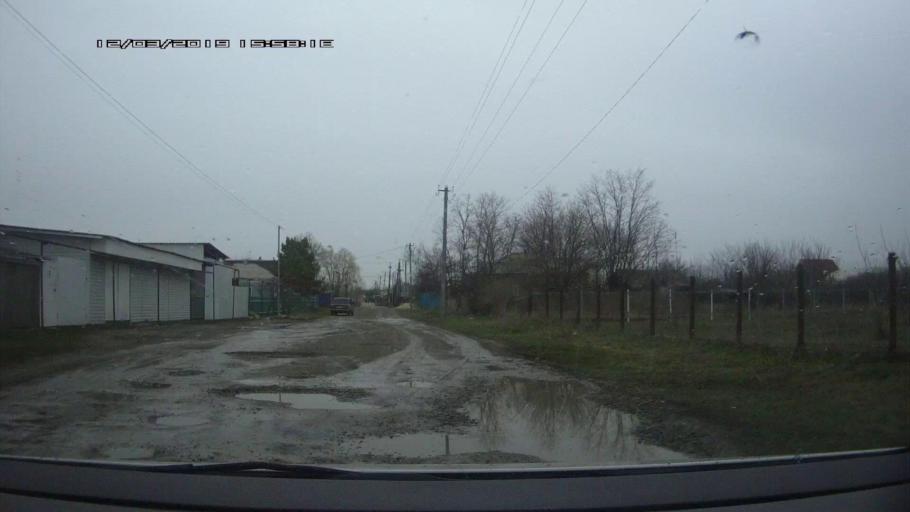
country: RU
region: Rostov
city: Novobataysk
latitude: 46.9025
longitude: 39.7894
